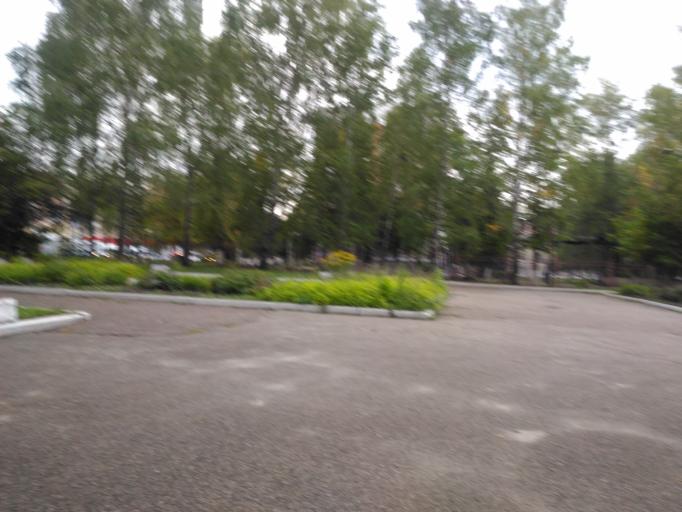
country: RU
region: Ulyanovsk
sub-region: Ulyanovskiy Rayon
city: Ulyanovsk
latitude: 54.2648
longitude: 48.3353
